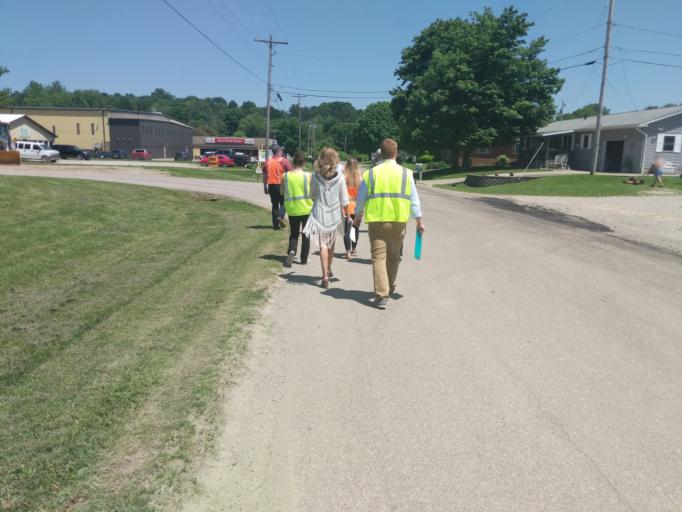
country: US
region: Ohio
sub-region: Washington County
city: Reno
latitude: 39.3938
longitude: -81.4029
